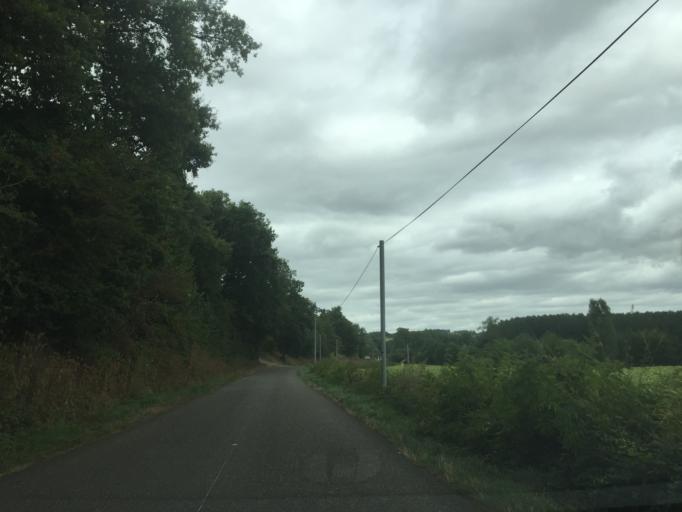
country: FR
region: Midi-Pyrenees
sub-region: Departement du Gers
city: Mirande
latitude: 43.6239
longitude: 0.3471
